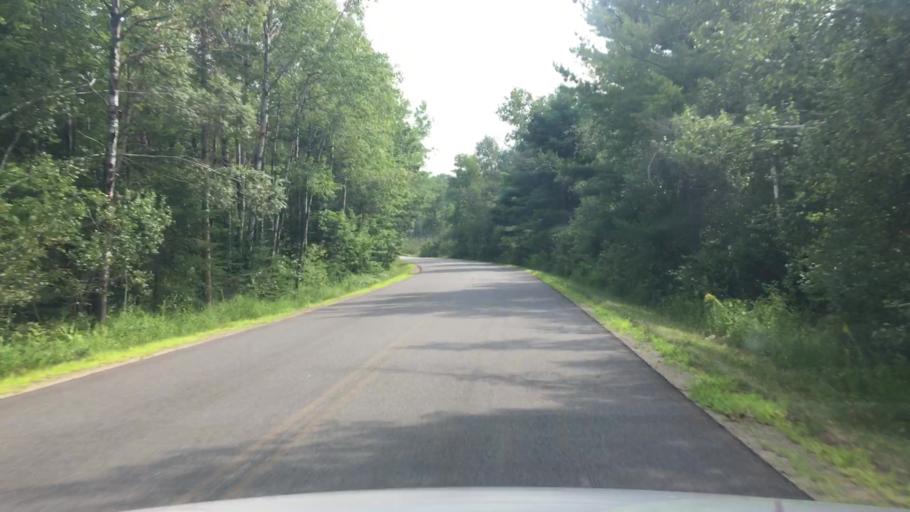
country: US
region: Maine
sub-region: Lincoln County
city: Jefferson
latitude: 44.2464
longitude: -69.4461
